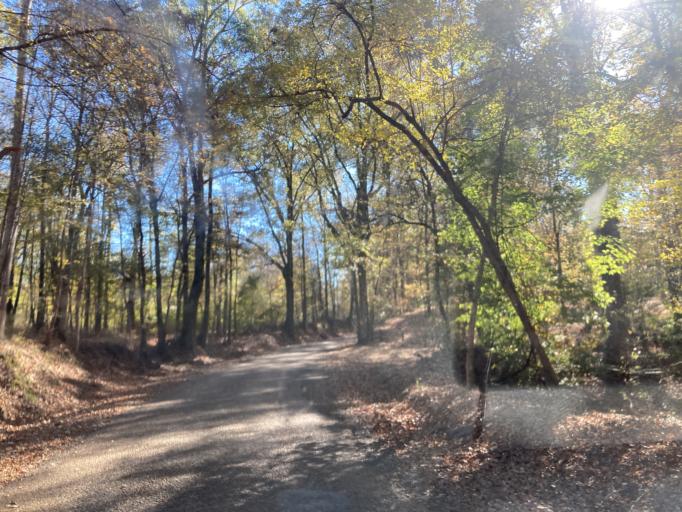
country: US
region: Mississippi
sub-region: Yazoo County
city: Yazoo City
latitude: 32.7790
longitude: -90.4069
